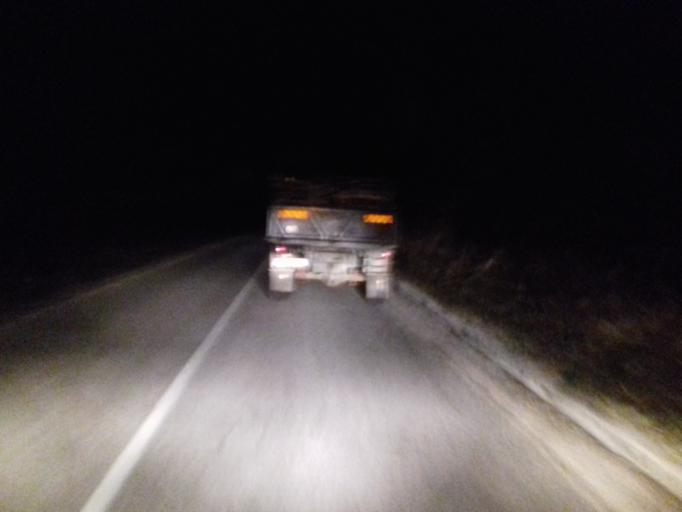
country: BA
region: Federation of Bosnia and Herzegovina
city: Gracanica
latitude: 43.7573
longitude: 18.3438
